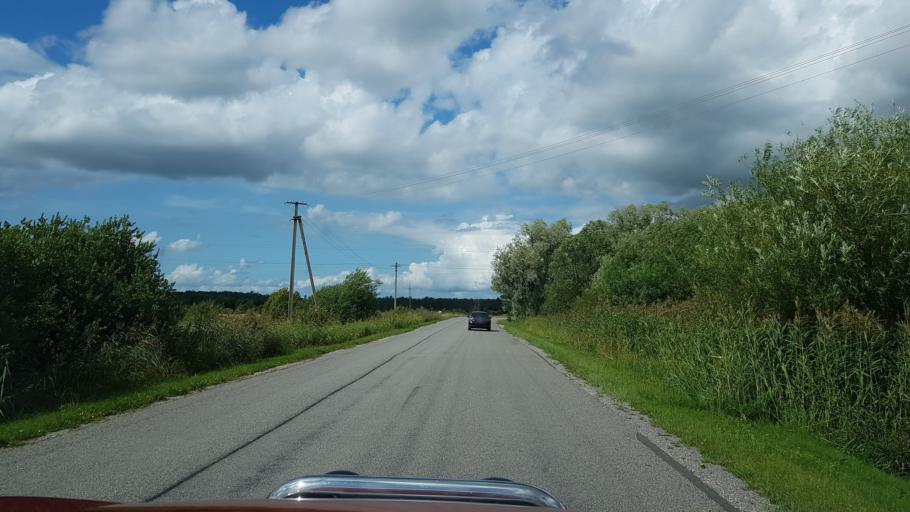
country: EE
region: Laeaene
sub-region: Lihula vald
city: Lihula
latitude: 58.6938
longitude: 23.8333
